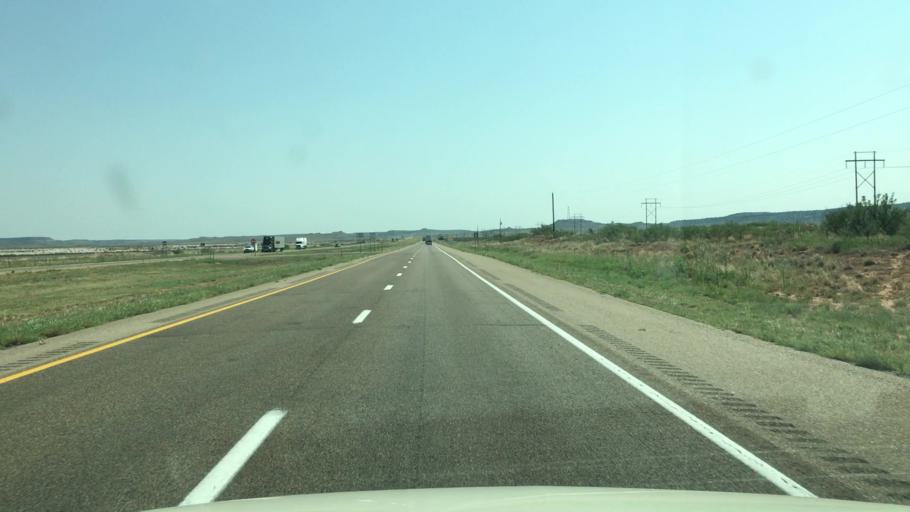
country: US
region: New Mexico
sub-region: Quay County
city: Tucumcari
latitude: 35.1148
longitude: -103.9928
